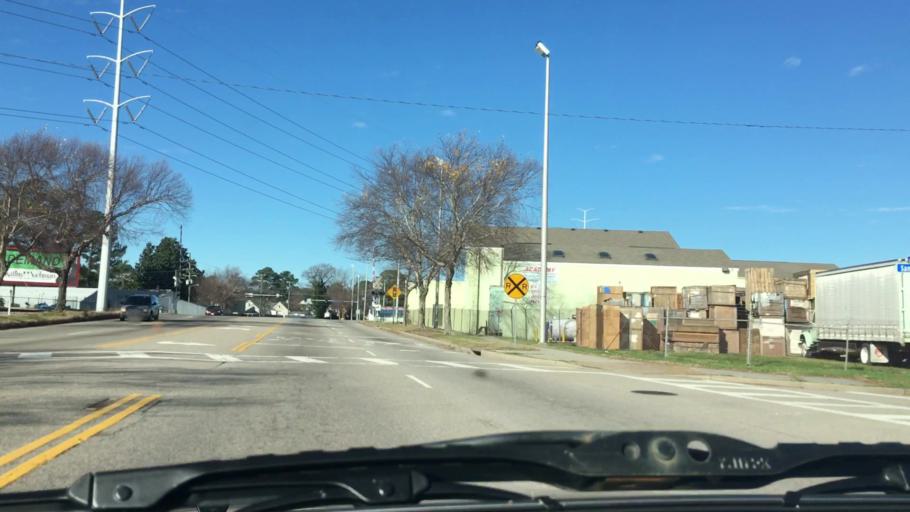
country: US
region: Virginia
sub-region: City of Norfolk
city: Norfolk
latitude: 36.8666
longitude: -76.2482
